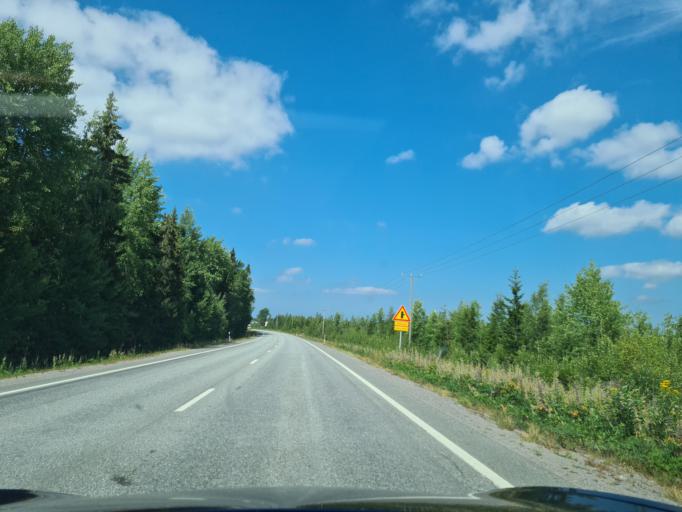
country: FI
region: Ostrobothnia
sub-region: Vaasa
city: Vaasa
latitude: 63.1634
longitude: 21.5909
